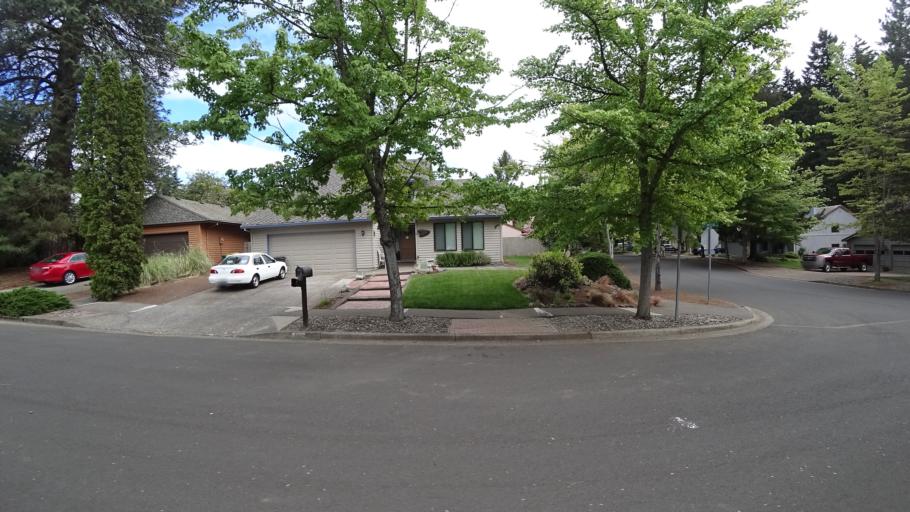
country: US
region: Oregon
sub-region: Washington County
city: Beaverton
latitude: 45.4720
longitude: -122.8130
